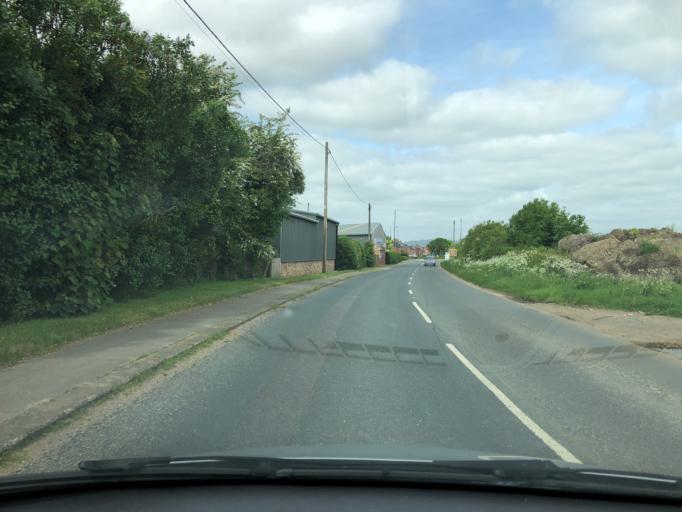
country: GB
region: England
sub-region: North Yorkshire
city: Thirsk
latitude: 54.2168
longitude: -1.3540
